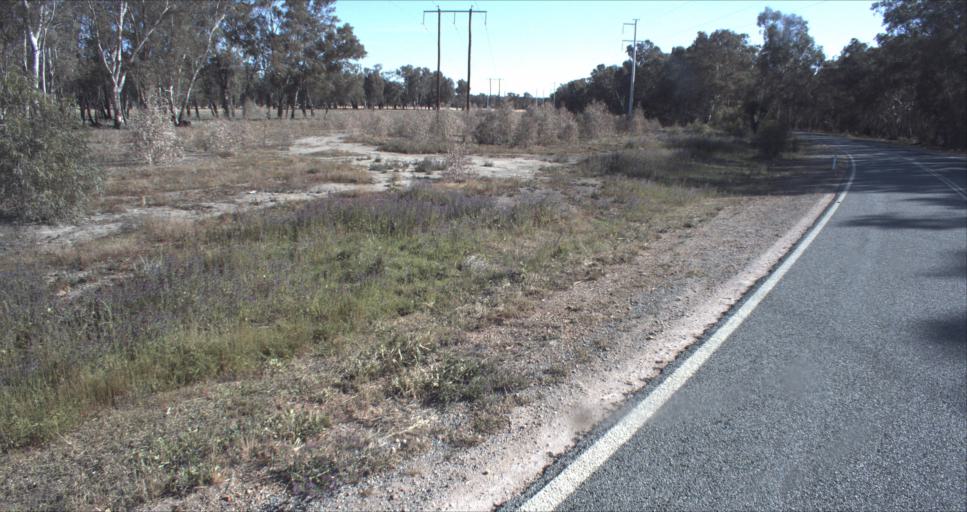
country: AU
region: New South Wales
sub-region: Leeton
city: Leeton
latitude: -34.6238
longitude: 146.3821
